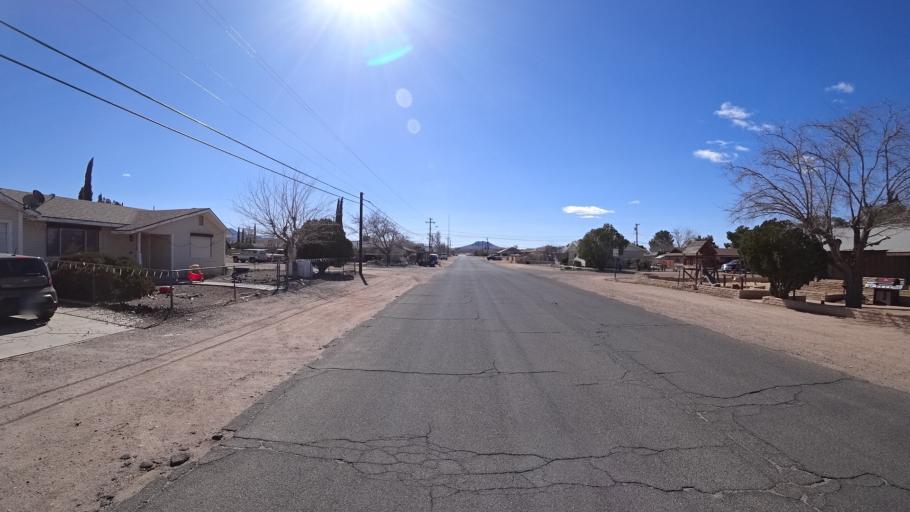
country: US
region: Arizona
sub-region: Mohave County
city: Kingman
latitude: 35.1943
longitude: -114.0201
